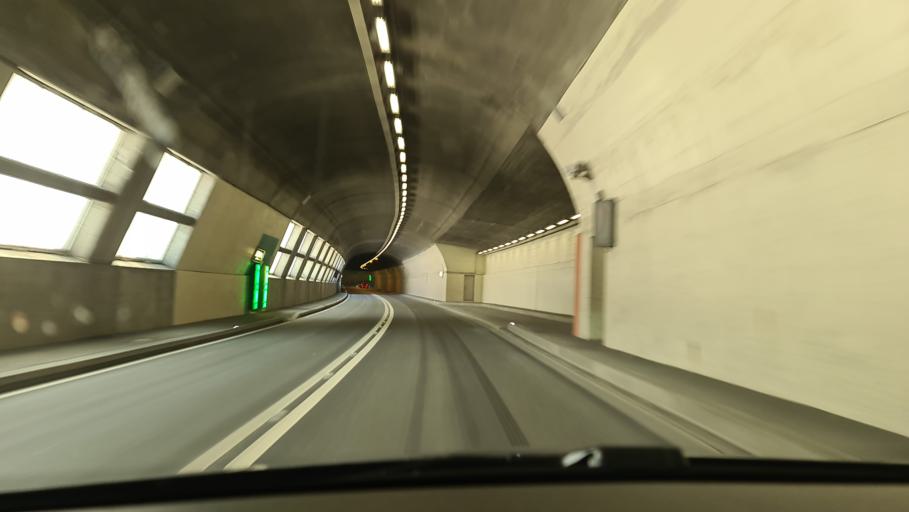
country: CH
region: Grisons
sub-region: Hinterrhein District
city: Hinterrhein
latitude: 46.5386
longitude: 9.2288
